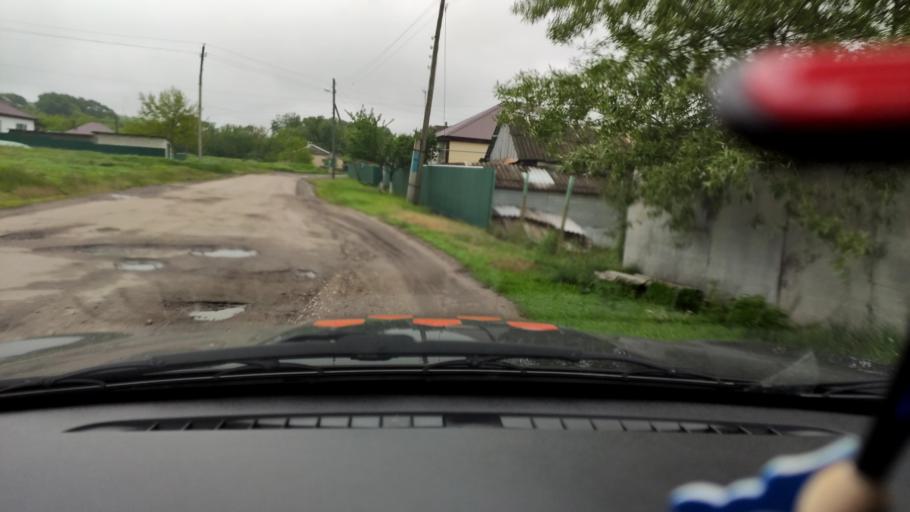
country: RU
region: Voronezj
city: Uryv-Pokrovka
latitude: 51.1182
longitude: 39.1630
